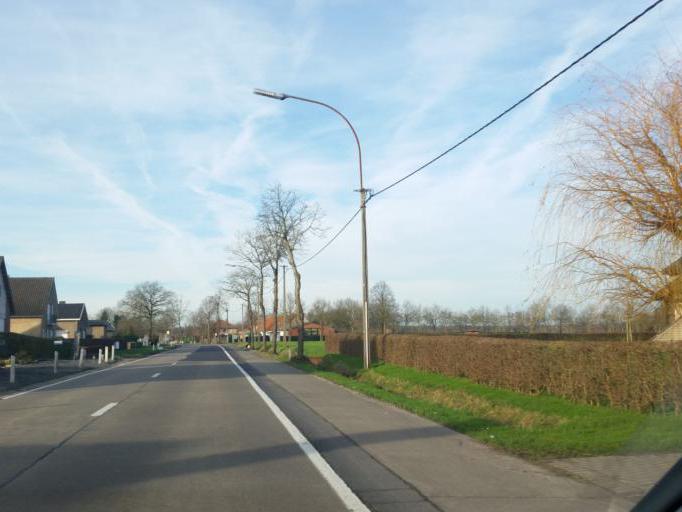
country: BE
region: Flanders
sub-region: Provincie Oost-Vlaanderen
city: Aalter
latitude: 51.1297
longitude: 3.4728
